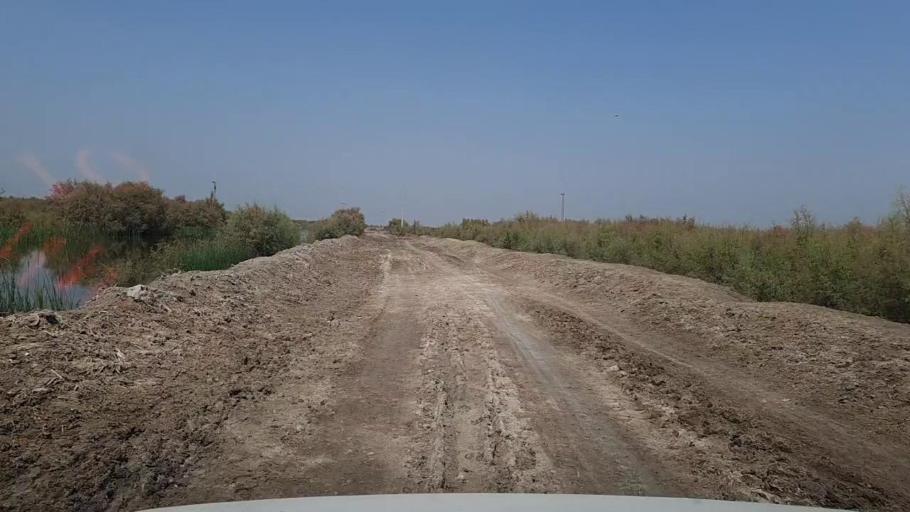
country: PK
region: Sindh
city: Kandhkot
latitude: 28.3441
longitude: 69.3020
